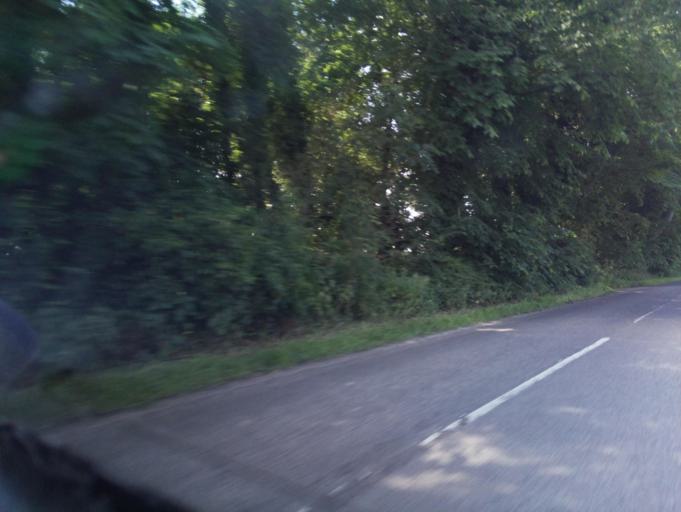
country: GB
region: England
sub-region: Derbyshire
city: Tideswell
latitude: 53.2611
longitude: -1.8109
